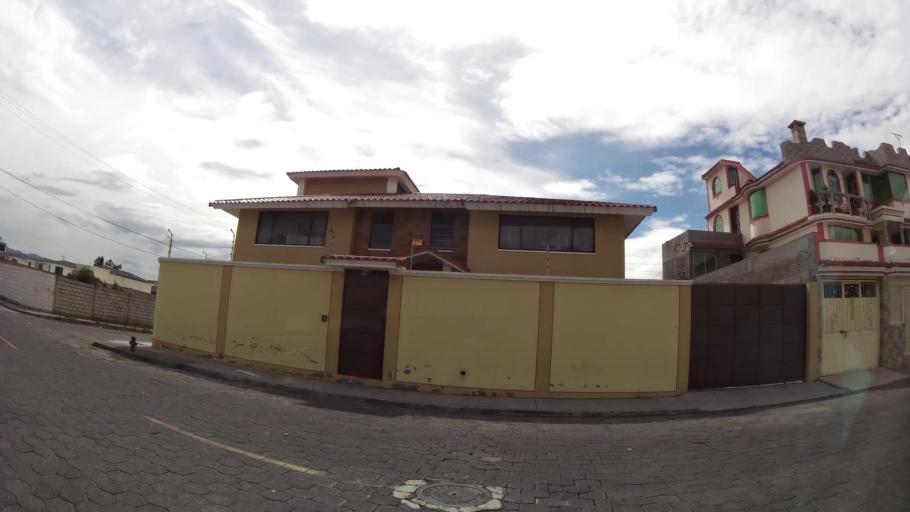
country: EC
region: Cotopaxi
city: Latacunga
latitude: -0.9324
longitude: -78.6019
